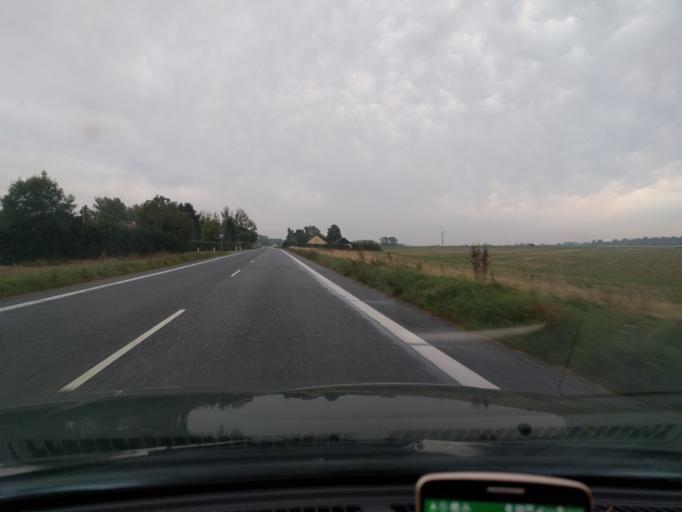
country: DK
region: Zealand
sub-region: Guldborgsund Kommune
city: Norre Alslev
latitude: 54.9375
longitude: 11.8671
